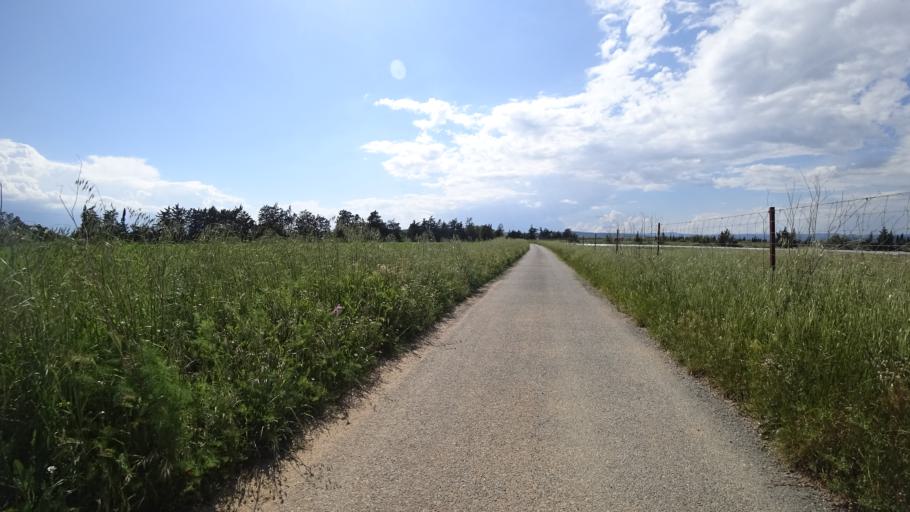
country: FR
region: Languedoc-Roussillon
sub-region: Departement de l'Aude
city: Ginestas
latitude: 43.2643
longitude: 2.8973
